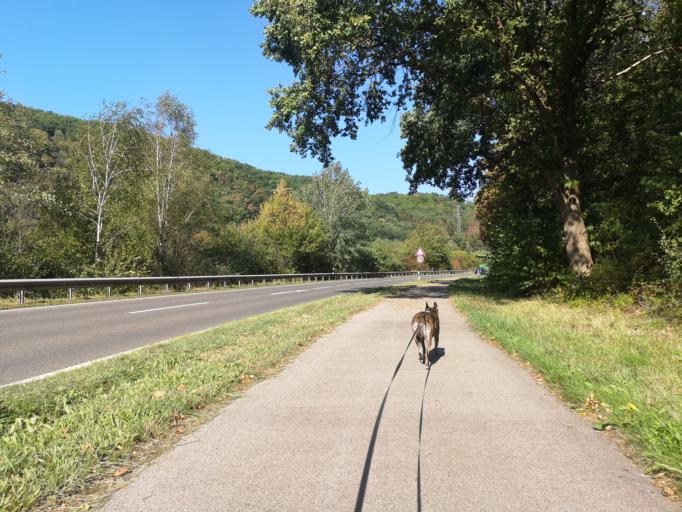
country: DE
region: North Rhine-Westphalia
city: Heimbach
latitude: 50.6483
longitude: 6.4770
